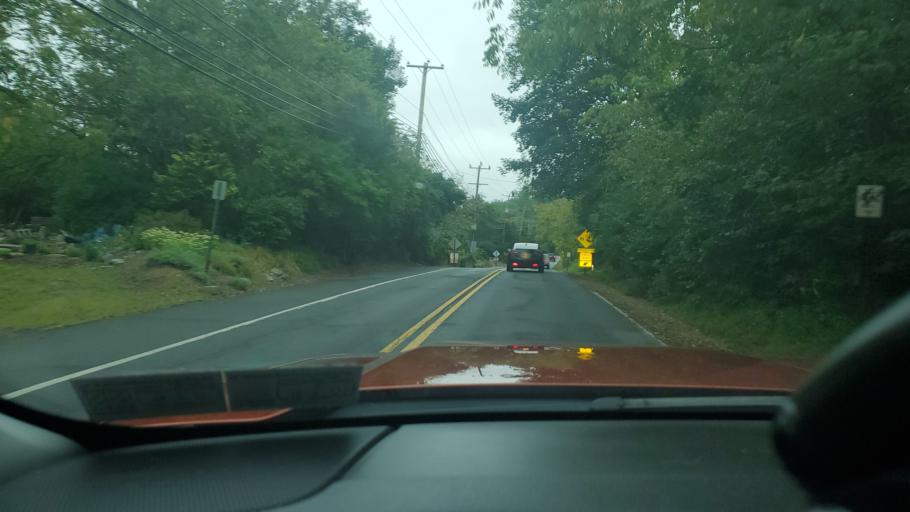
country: US
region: Pennsylvania
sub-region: Montgomery County
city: Woxall
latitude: 40.3245
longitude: -75.4778
